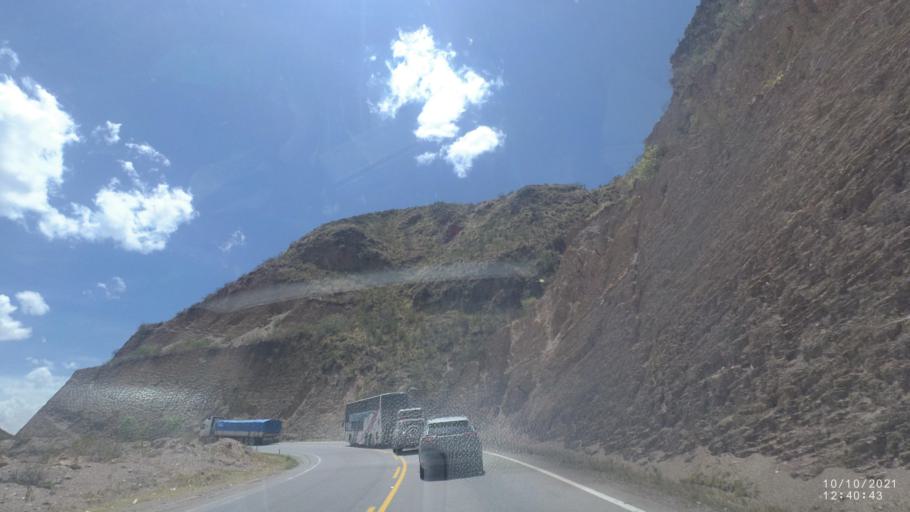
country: BO
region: Cochabamba
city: Irpa Irpa
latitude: -17.6385
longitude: -66.3881
